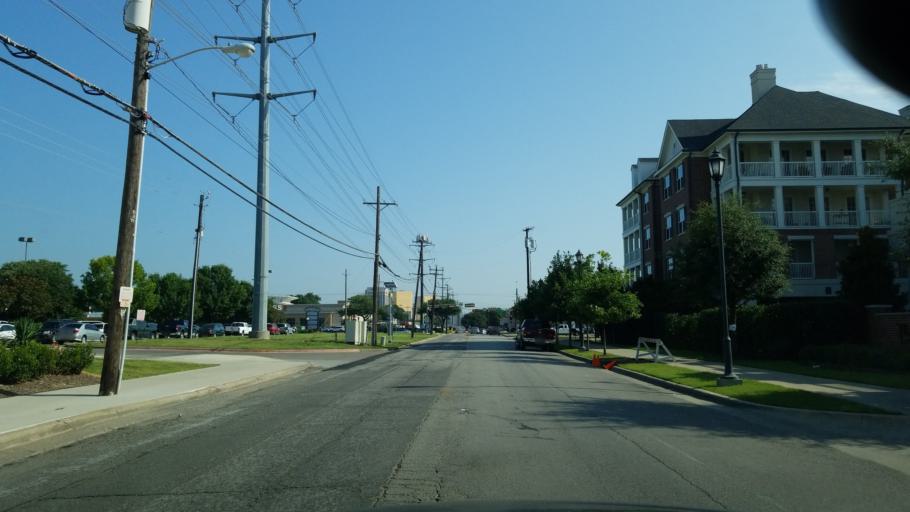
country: US
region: Texas
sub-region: Dallas County
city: Highland Park
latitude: 32.8496
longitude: -96.7677
